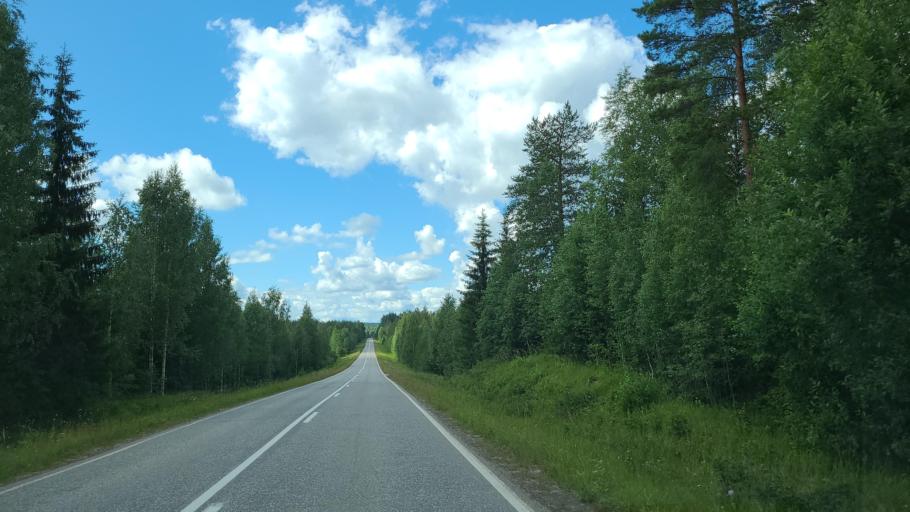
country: FI
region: Northern Savo
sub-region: Koillis-Savo
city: Kaavi
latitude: 62.9823
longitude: 28.8056
